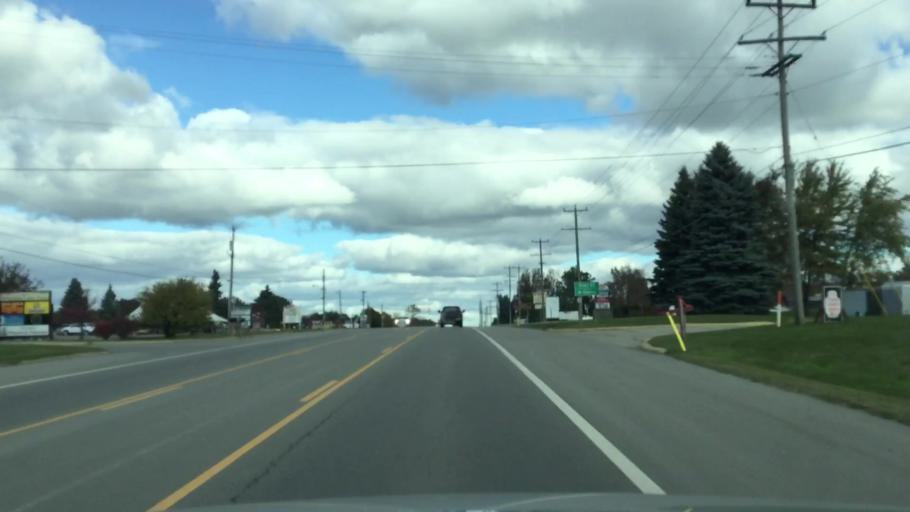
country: US
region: Michigan
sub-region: Lapeer County
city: Lapeer
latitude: 42.9535
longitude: -83.3138
